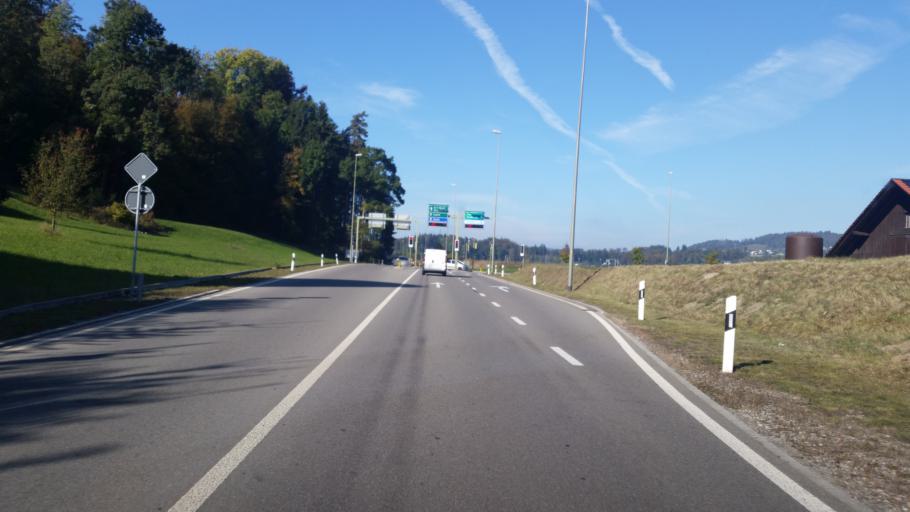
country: CH
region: Zurich
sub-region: Bezirk Affoltern
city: Wettswil / Wettswil (Dorf)
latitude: 47.3336
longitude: 8.4595
